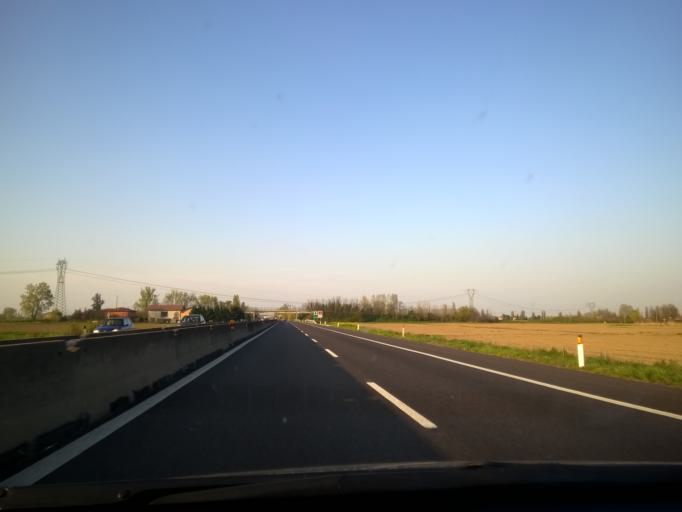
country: IT
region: Emilia-Romagna
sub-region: Provincia di Bologna
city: Bentivoglio
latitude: 44.6045
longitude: 11.4090
